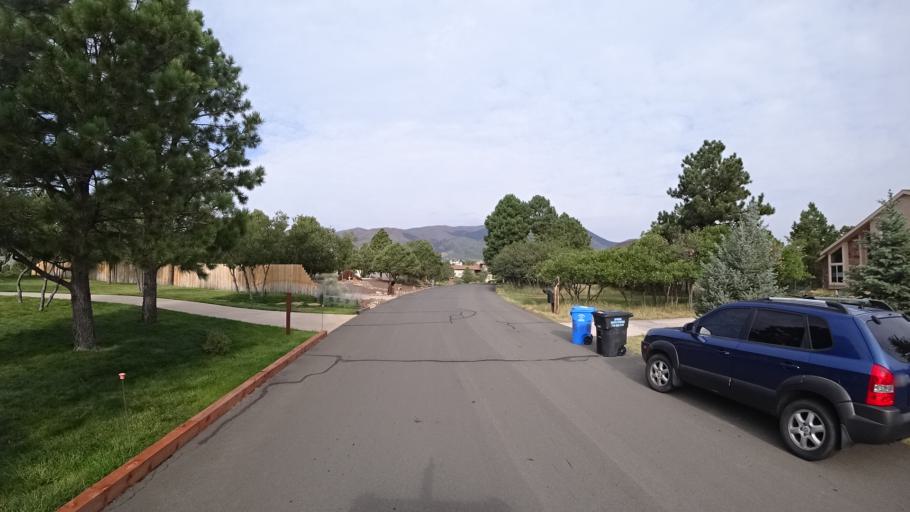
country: US
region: Colorado
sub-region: El Paso County
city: Air Force Academy
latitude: 38.9329
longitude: -104.8549
